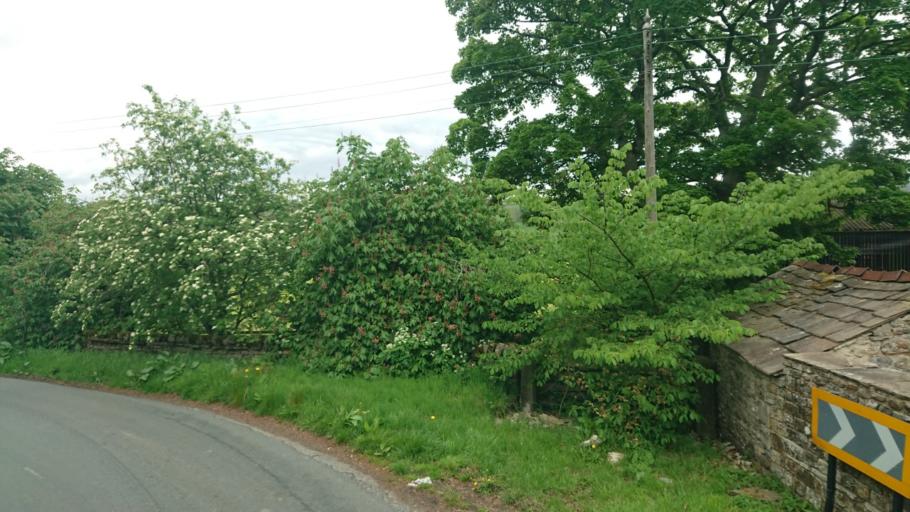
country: GB
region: England
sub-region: North Yorkshire
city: Leyburn
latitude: 54.2791
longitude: -1.9739
